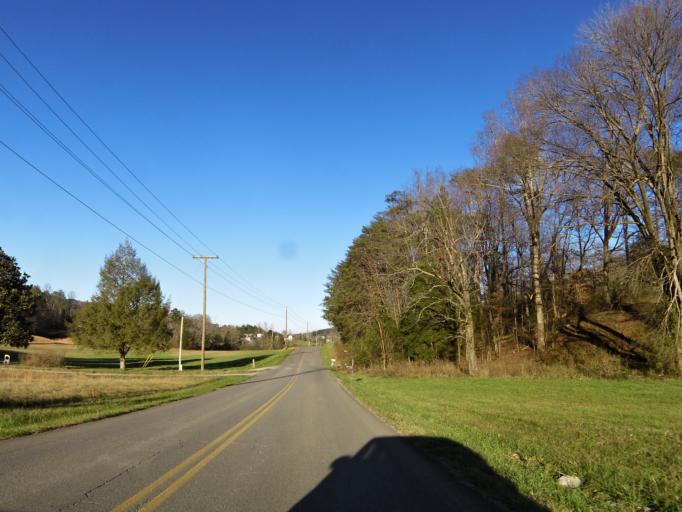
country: US
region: Tennessee
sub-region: Anderson County
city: Clinton
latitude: 36.1058
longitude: -84.2175
